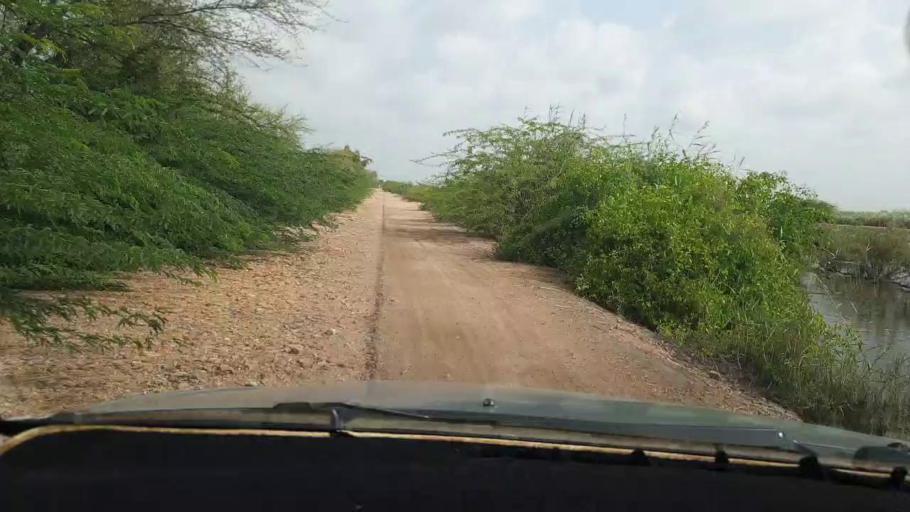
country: PK
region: Sindh
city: Tando Bago
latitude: 24.7778
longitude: 69.0260
